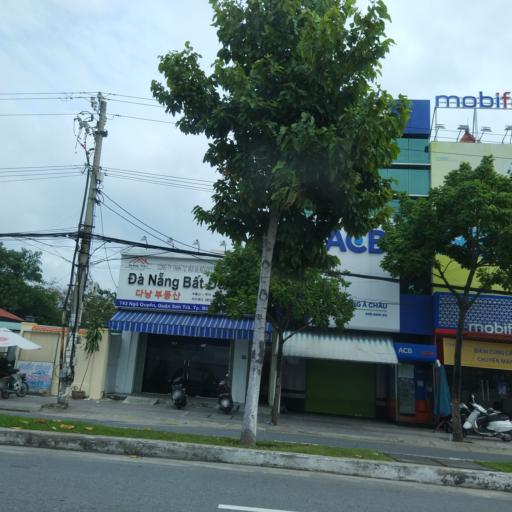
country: VN
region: Da Nang
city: Son Tra
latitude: 16.0704
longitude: 108.2315
